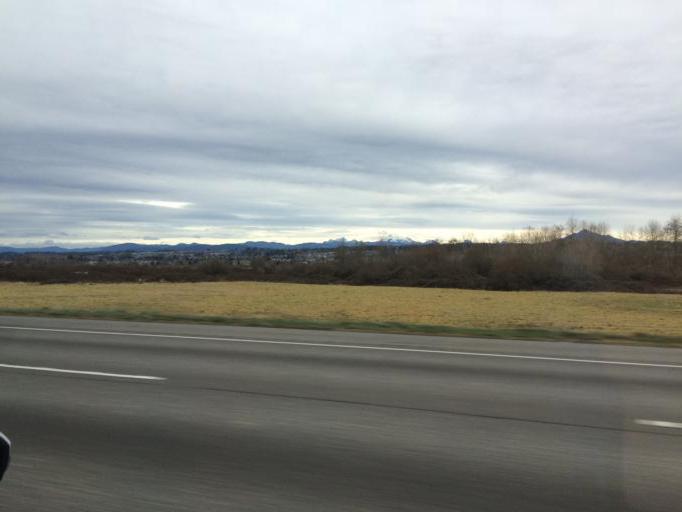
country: US
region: Washington
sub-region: Snohomish County
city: Marysville
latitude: 48.0308
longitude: -122.1771
